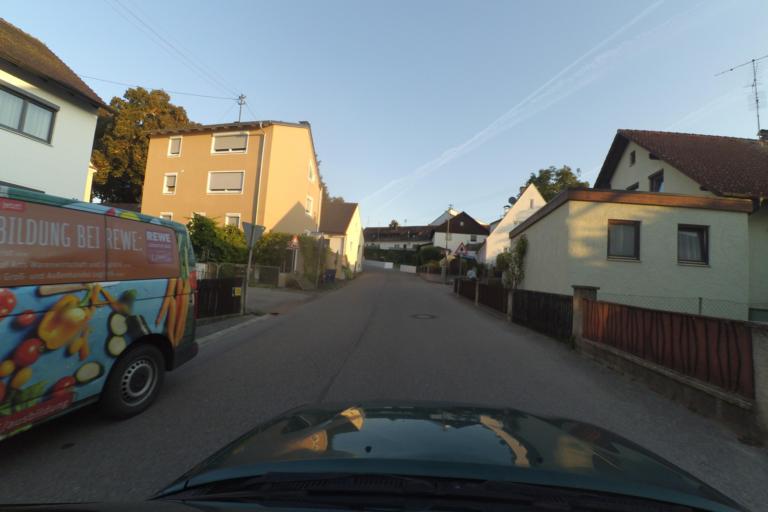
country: DE
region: Bavaria
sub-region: Lower Bavaria
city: Mainburg
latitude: 48.6448
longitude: 11.7801
